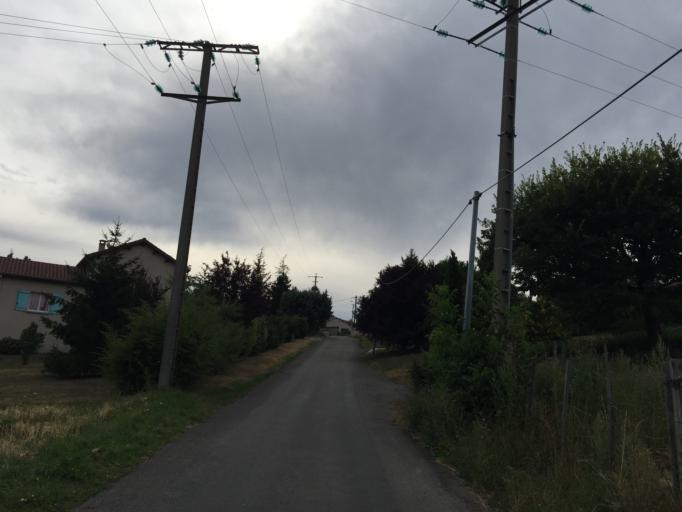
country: FR
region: Rhone-Alpes
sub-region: Departement de la Loire
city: Sorbiers
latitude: 45.4930
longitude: 4.4787
